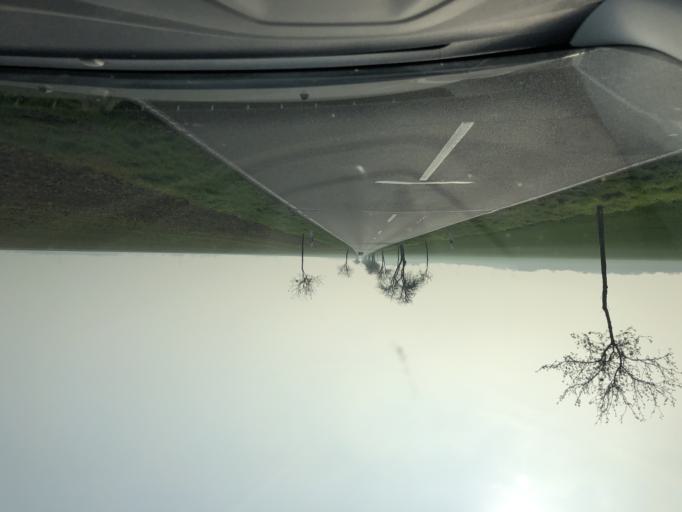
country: DE
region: Saxony-Anhalt
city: Brehna
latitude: 51.5910
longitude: 12.1667
